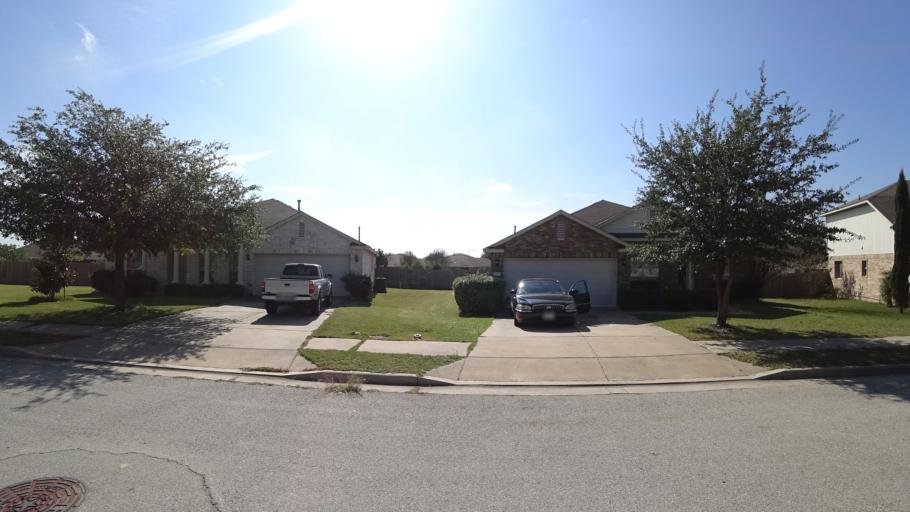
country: US
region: Texas
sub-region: Travis County
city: Pflugerville
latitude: 30.4196
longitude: -97.6336
